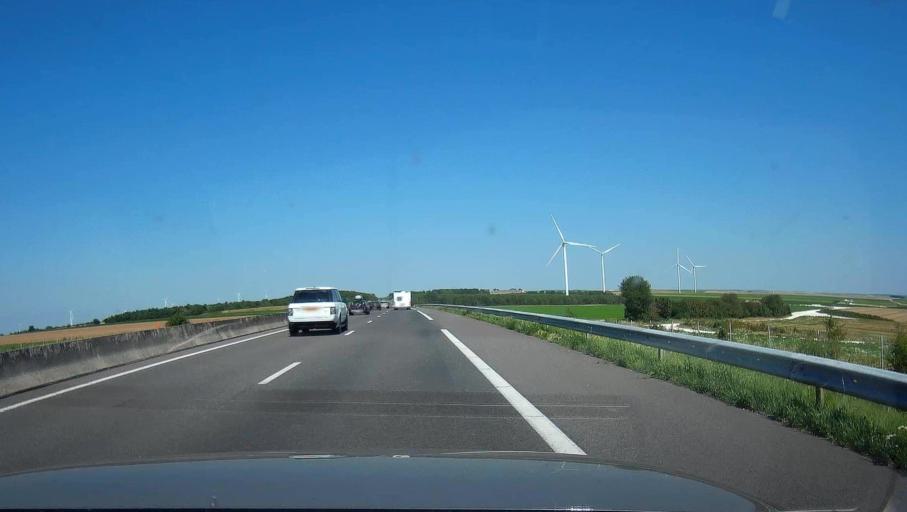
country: FR
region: Champagne-Ardenne
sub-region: Departement de l'Aube
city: Mailly-le-Camp
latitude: 48.6237
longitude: 4.1825
